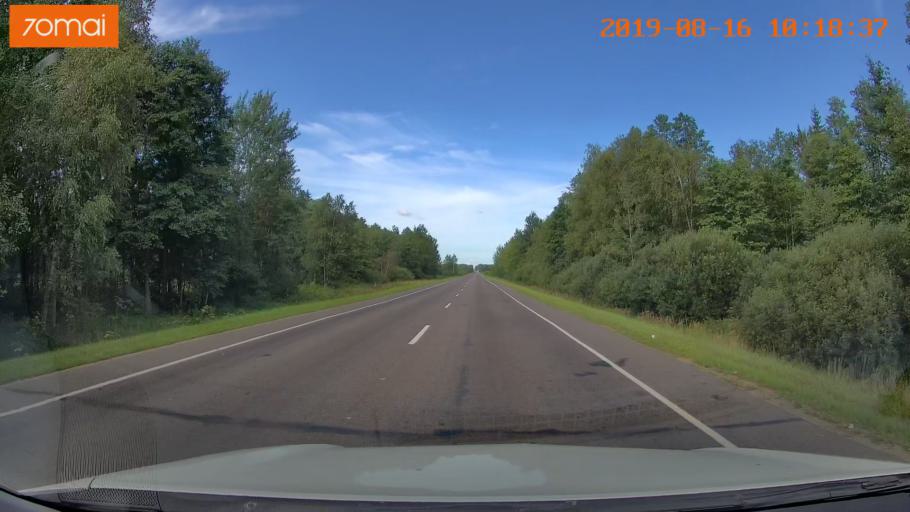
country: BY
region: Mogilev
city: Asipovichy
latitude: 53.3060
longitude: 28.6860
